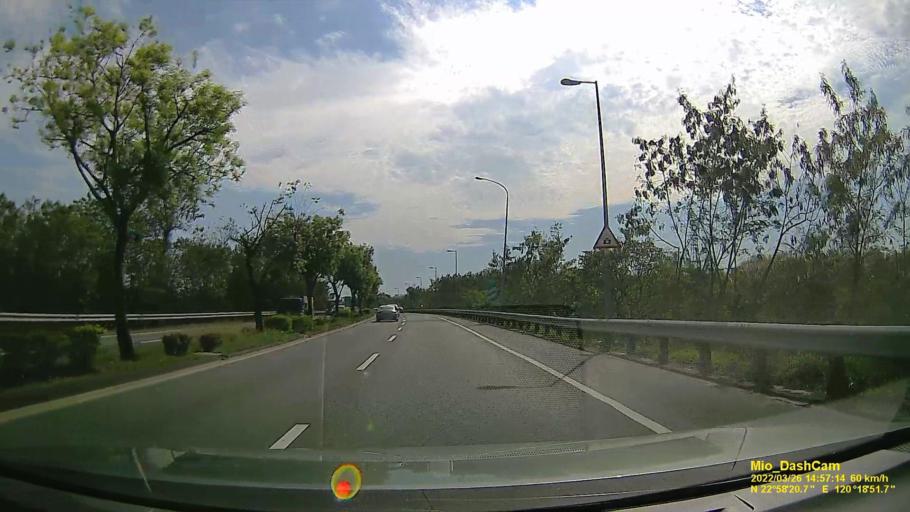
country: TW
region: Taiwan
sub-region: Tainan
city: Tainan
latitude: 22.9724
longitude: 120.3144
